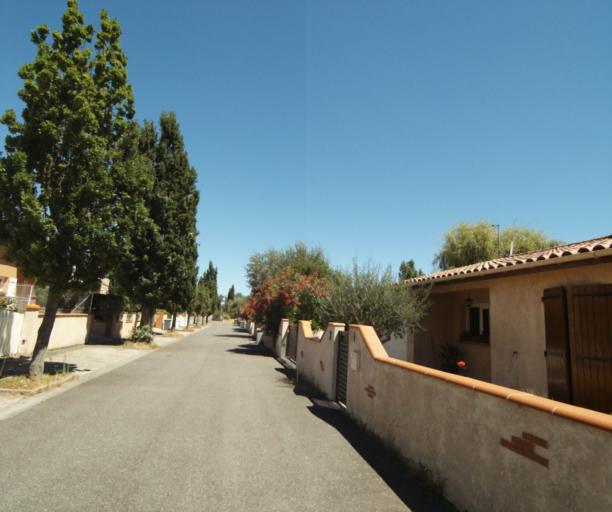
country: FR
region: Midi-Pyrenees
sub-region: Departement de la Haute-Garonne
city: Pechabou
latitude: 43.5121
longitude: 1.5133
